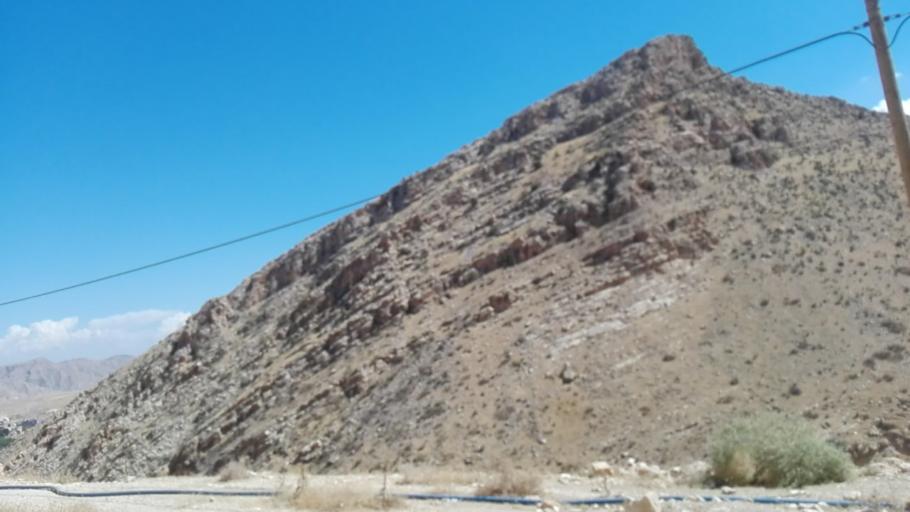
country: TR
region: Batman
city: Hasankeyf
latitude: 37.6992
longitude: 41.4587
